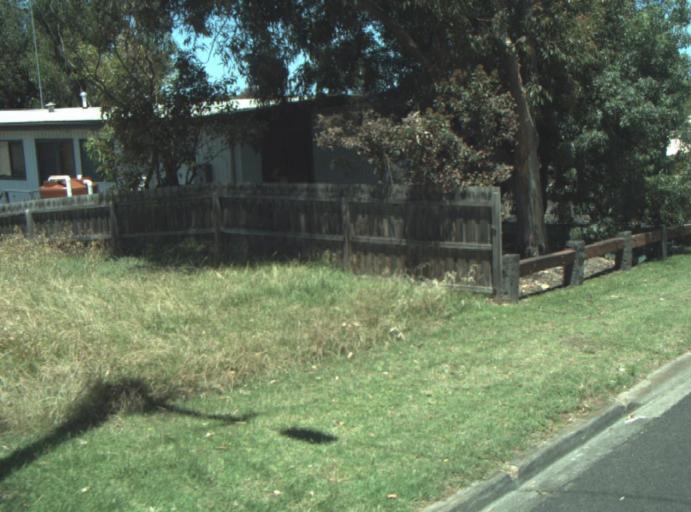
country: AU
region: Victoria
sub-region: Greater Geelong
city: Clifton Springs
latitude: -38.2635
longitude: 144.5486
